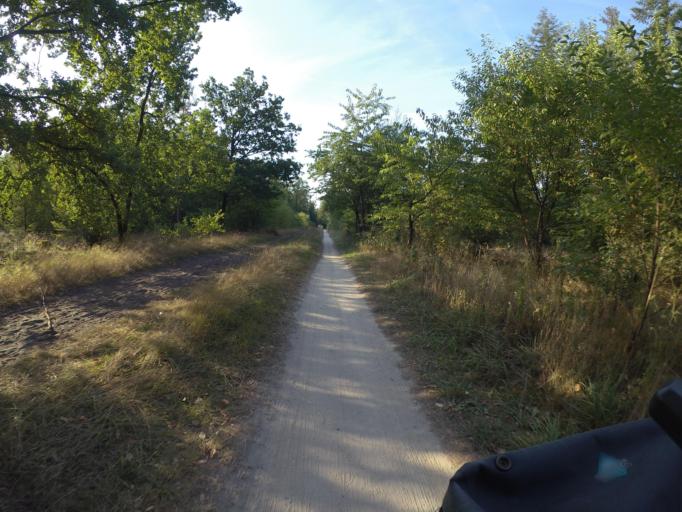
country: NL
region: Drenthe
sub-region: Gemeente Westerveld
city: Dwingeloo
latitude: 52.9292
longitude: 6.3322
